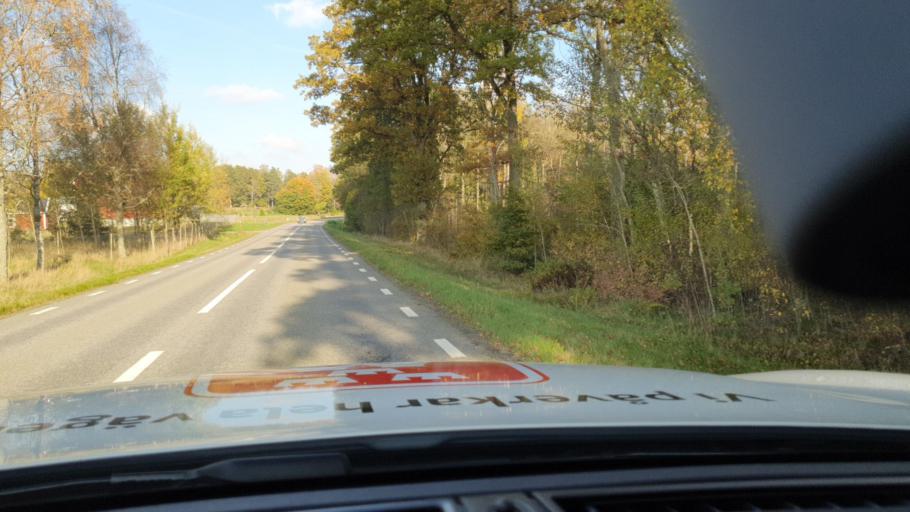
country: SE
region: Kronoberg
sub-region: Ljungby Kommun
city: Ljungby
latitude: 56.8224
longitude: 13.8054
